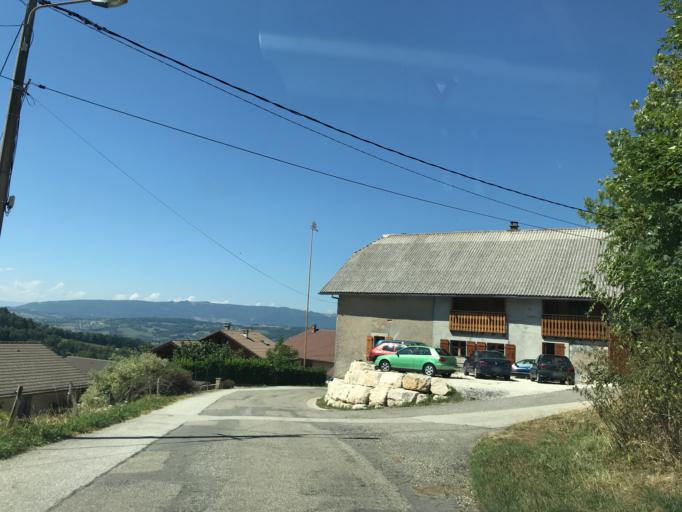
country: FR
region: Rhone-Alpes
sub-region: Departement de la Haute-Savoie
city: Thorens-Glieres
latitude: 45.9782
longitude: 6.2287
